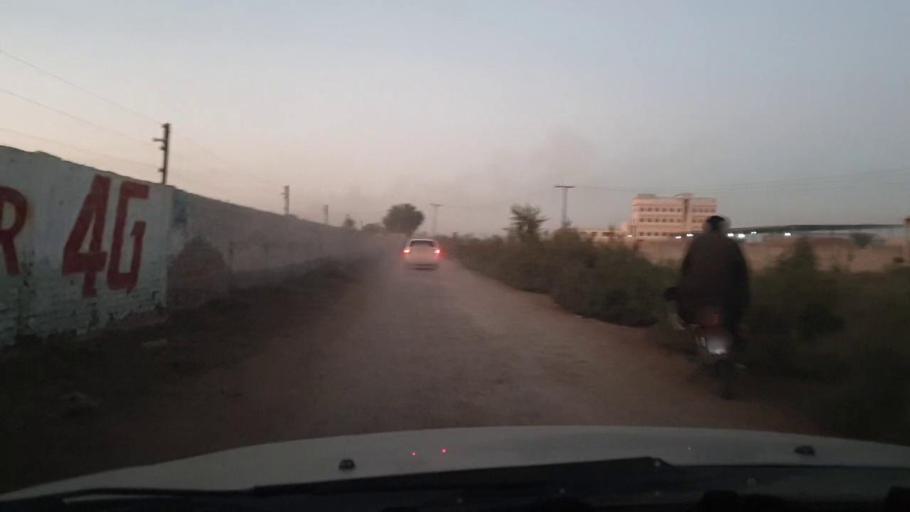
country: PK
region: Sindh
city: Ghotki
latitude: 27.9827
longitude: 69.2870
